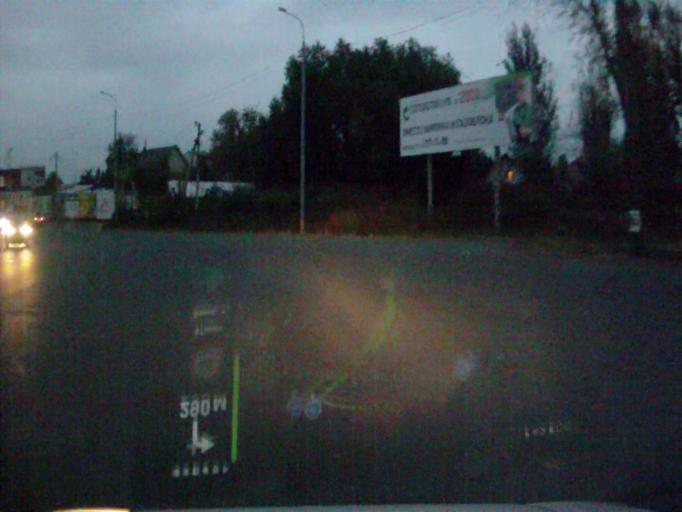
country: RU
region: Chelyabinsk
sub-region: Gorod Chelyabinsk
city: Chelyabinsk
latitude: 55.1565
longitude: 61.2990
